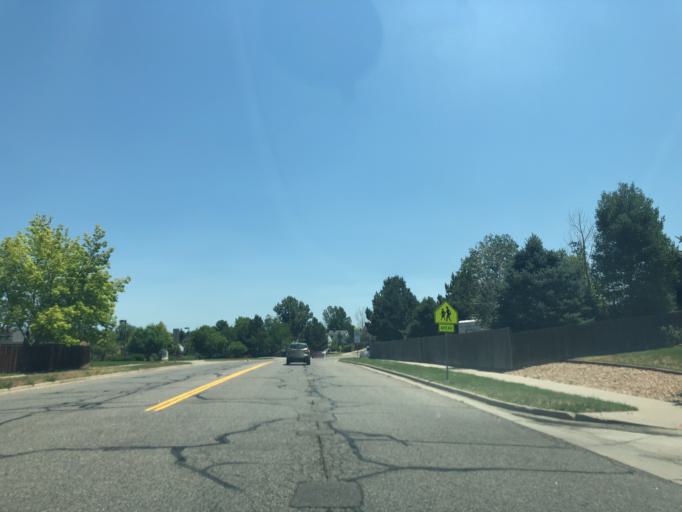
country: US
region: Colorado
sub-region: Arapahoe County
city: Dove Valley
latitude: 39.6272
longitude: -104.7630
